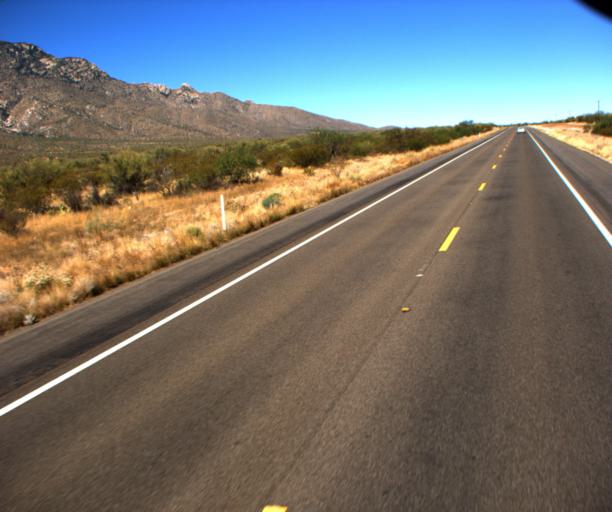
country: US
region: Arizona
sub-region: Pima County
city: Three Points
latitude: 32.0393
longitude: -111.4955
